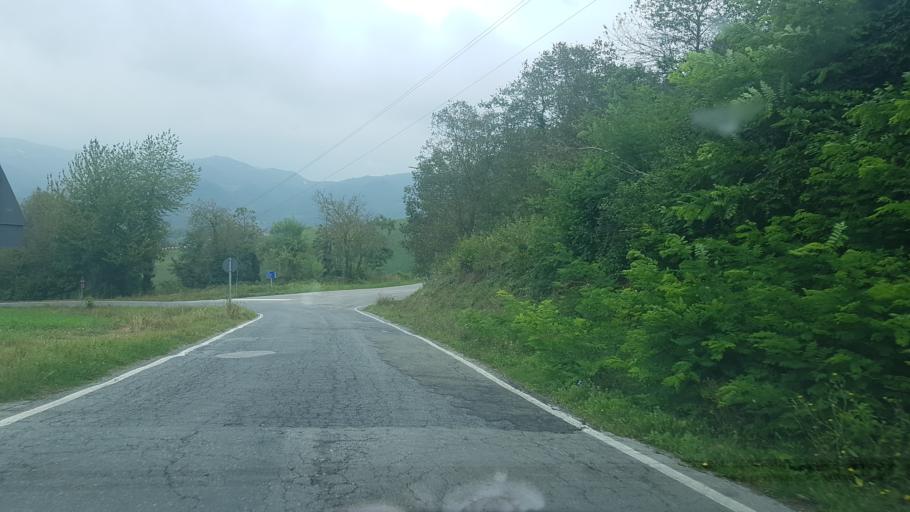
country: IT
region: Piedmont
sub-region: Provincia di Cuneo
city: Camerana
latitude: 44.4224
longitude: 8.1431
